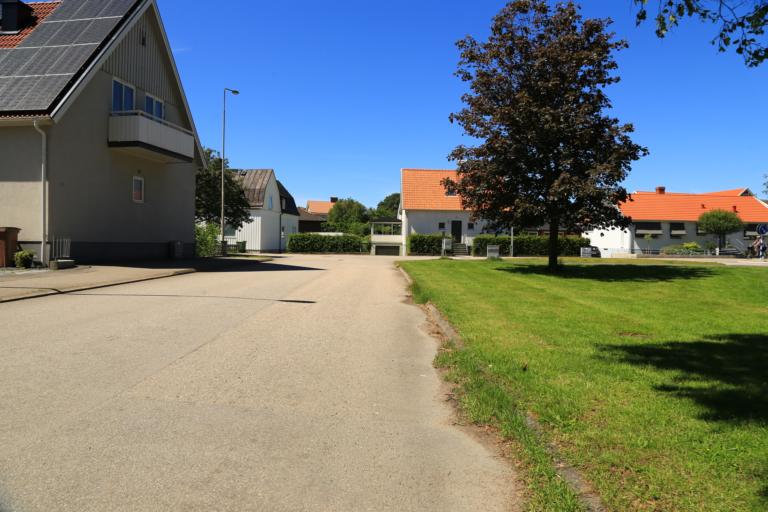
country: SE
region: Halland
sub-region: Varbergs Kommun
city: Varberg
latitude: 57.1043
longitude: 12.2618
